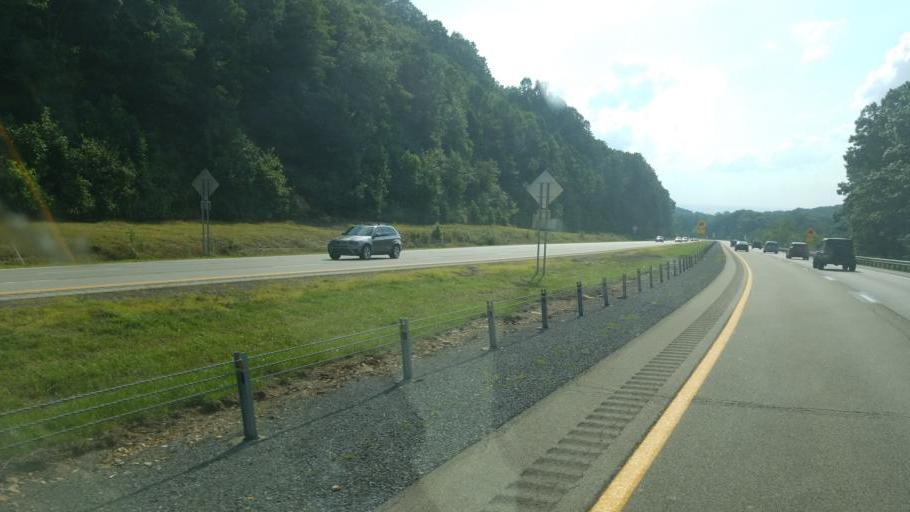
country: US
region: West Virginia
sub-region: Monongalia County
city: Cheat Lake
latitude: 39.6611
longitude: -79.7974
